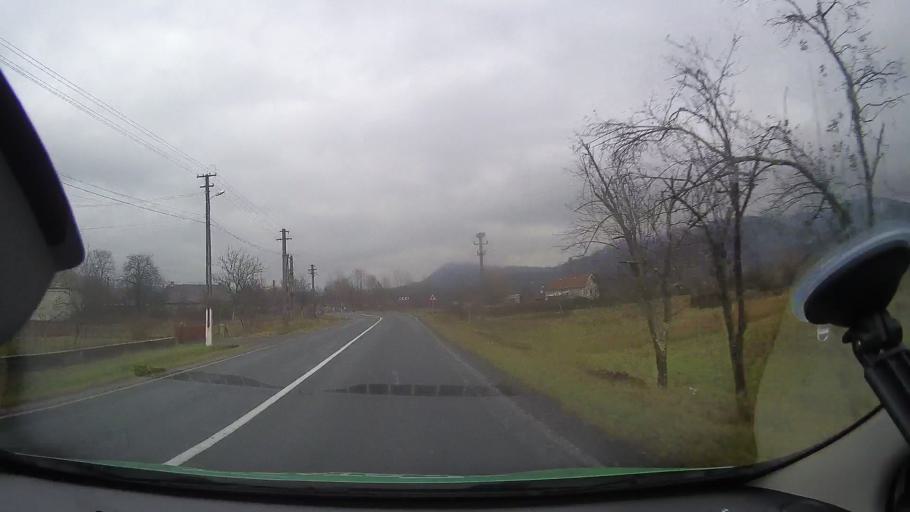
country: RO
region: Arad
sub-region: Comuna Plescuta
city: Plescuta
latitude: 46.2925
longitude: 22.4006
